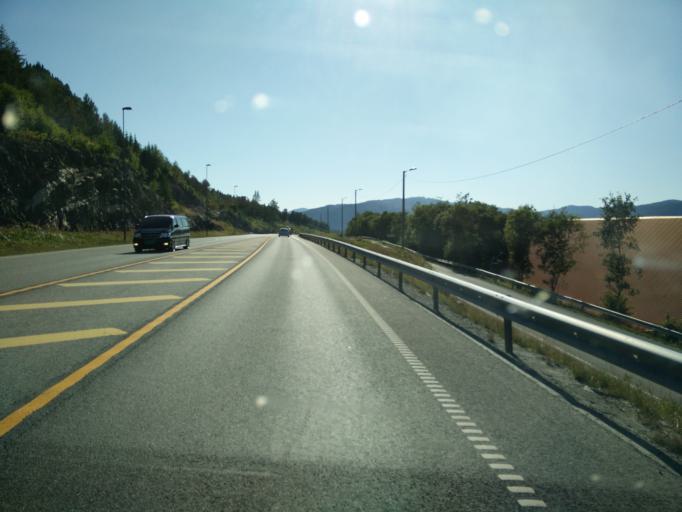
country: NO
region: Sor-Trondelag
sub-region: Orkdal
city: Orkanger
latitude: 63.3195
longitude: 9.8826
